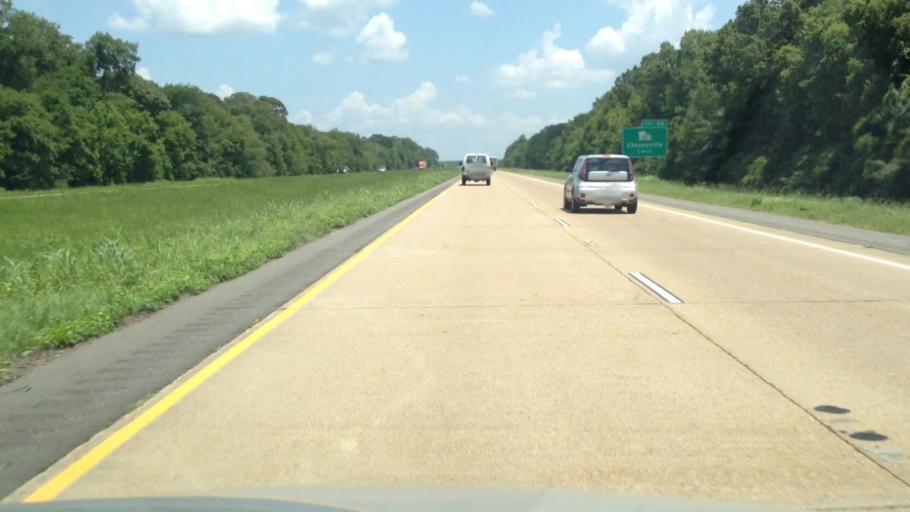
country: US
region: Louisiana
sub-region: Rapides Parish
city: Lecompte
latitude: 30.9964
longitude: -92.3303
